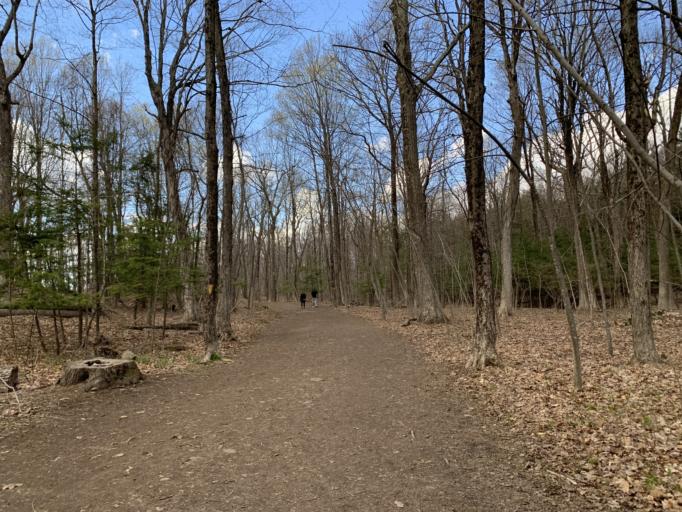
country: US
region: Connecticut
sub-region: Hartford County
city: Weatogue
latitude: 41.8338
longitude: -72.7975
